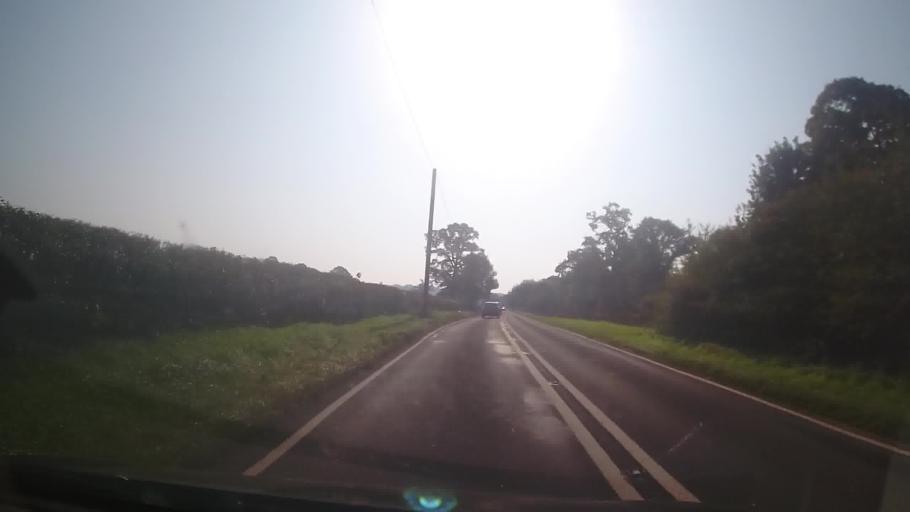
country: GB
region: England
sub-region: Shropshire
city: Alveley
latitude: 52.4991
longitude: -2.3716
